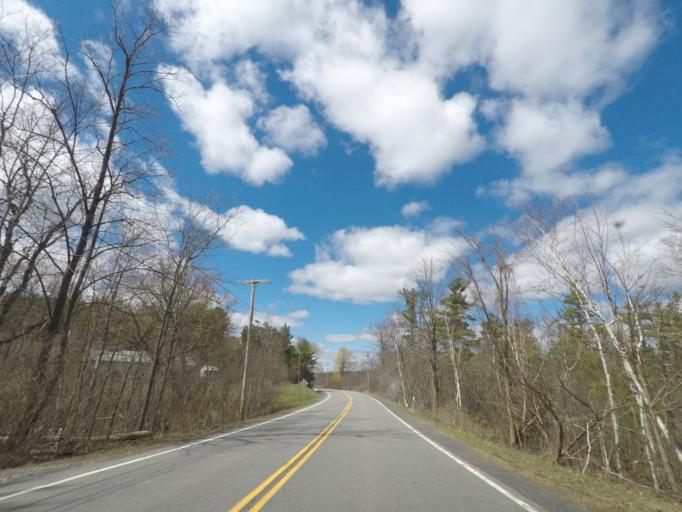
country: US
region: New York
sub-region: Albany County
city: Voorheesville
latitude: 42.6454
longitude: -73.9731
